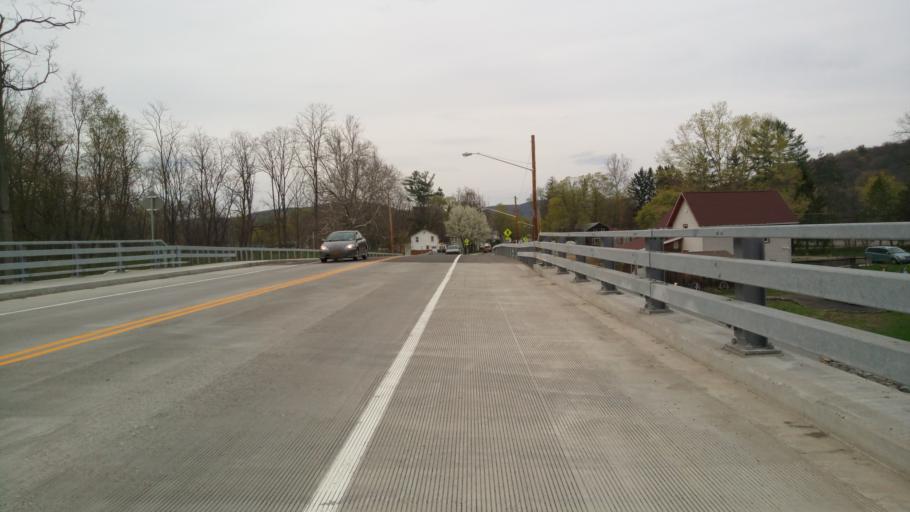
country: US
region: New York
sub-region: Chemung County
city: Southport
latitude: 42.0092
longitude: -76.7293
